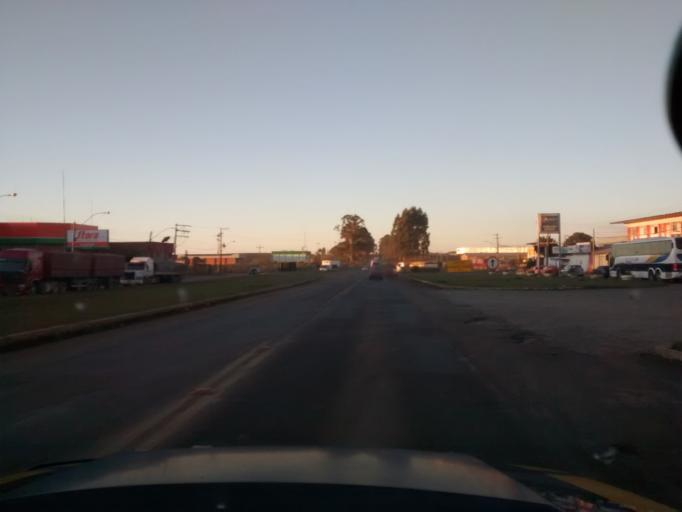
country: BR
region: Rio Grande do Sul
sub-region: Vacaria
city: Vacaria
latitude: -28.4996
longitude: -50.9187
